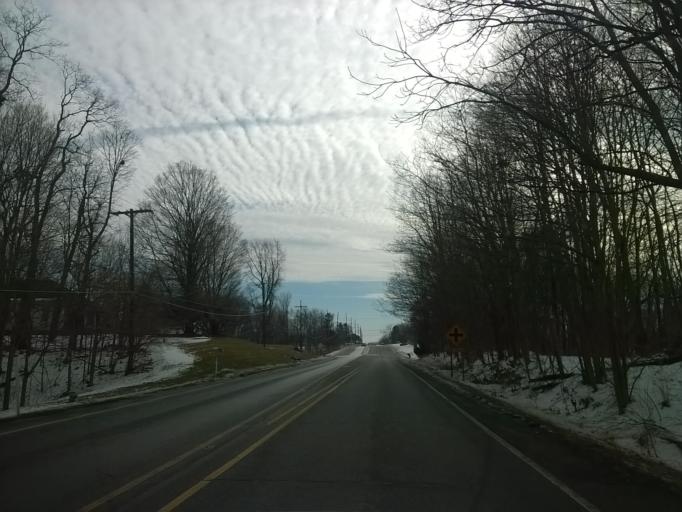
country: US
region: Indiana
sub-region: Boone County
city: Zionsville
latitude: 39.9655
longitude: -86.2488
